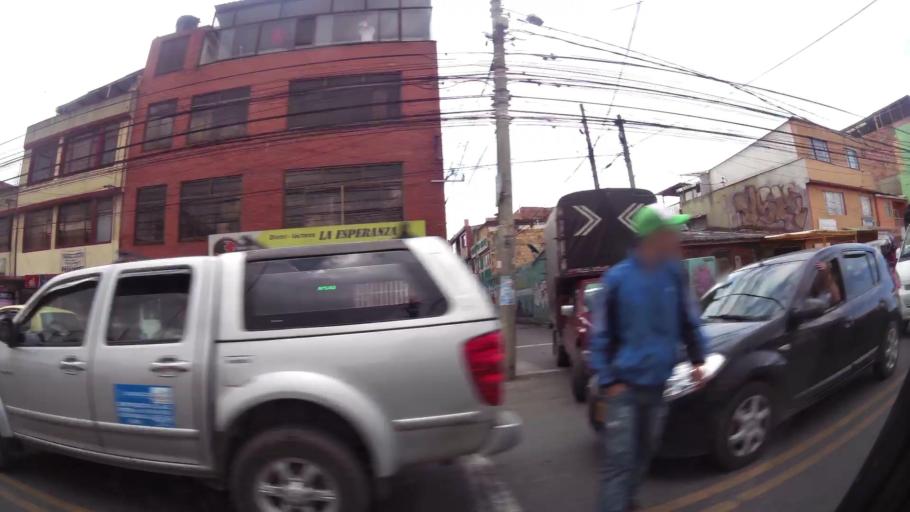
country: CO
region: Cundinamarca
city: Cota
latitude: 4.7412
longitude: -74.0971
